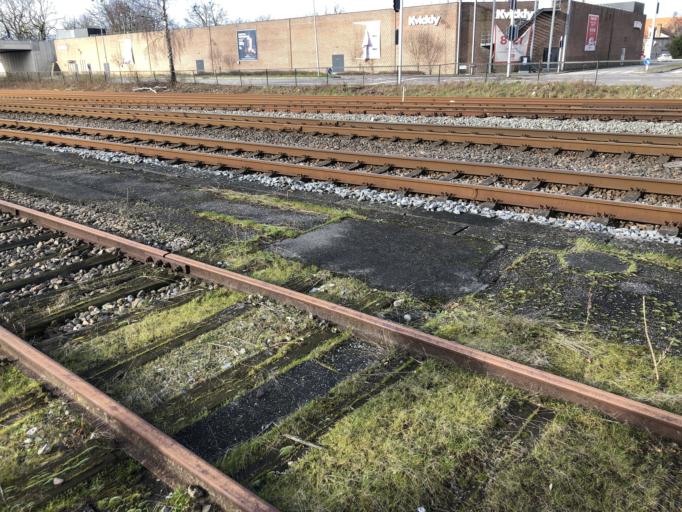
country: DK
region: Zealand
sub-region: Guldborgsund Kommune
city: Nykobing Falster
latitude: 54.7647
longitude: 11.8756
